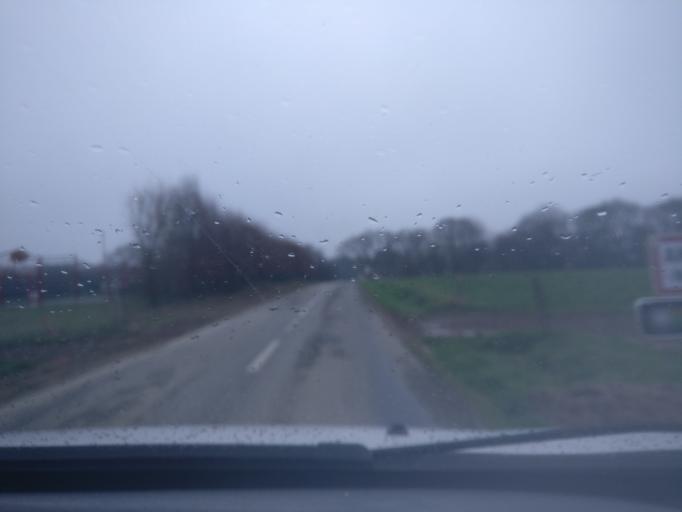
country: FR
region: Brittany
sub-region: Departement d'Ille-et-Vilaine
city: Chasne-sur-Illet
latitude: 48.2978
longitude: -1.5884
